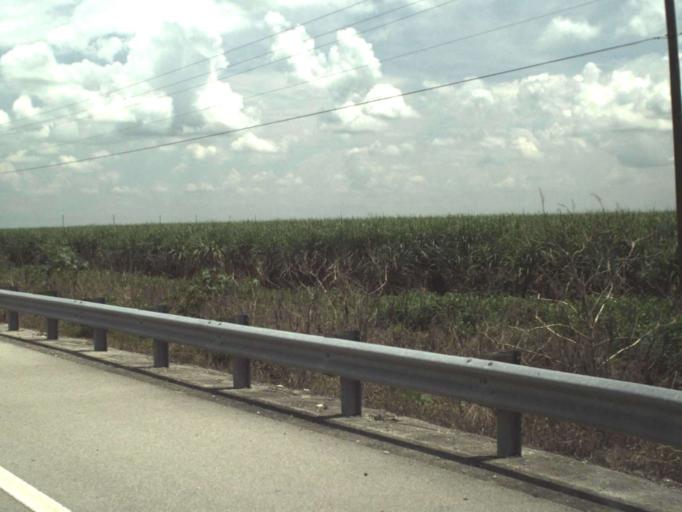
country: US
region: Florida
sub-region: Palm Beach County
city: Pahokee
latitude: 26.8065
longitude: -80.5552
